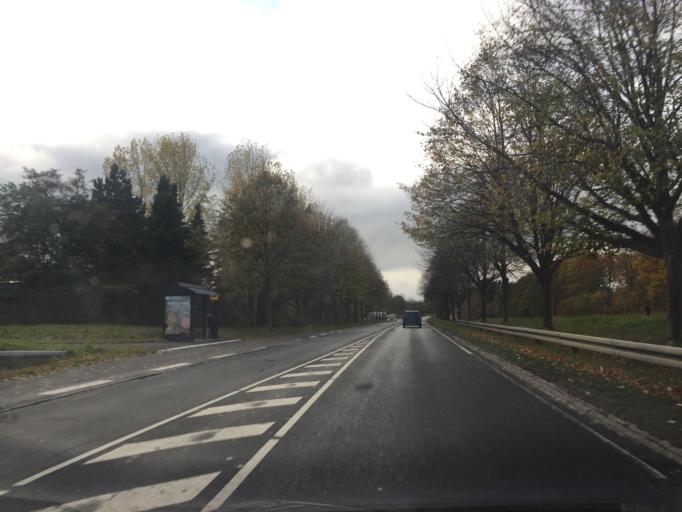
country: DK
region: Capital Region
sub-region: Fredensborg Kommune
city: Humlebaek
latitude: 55.9653
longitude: 12.5208
